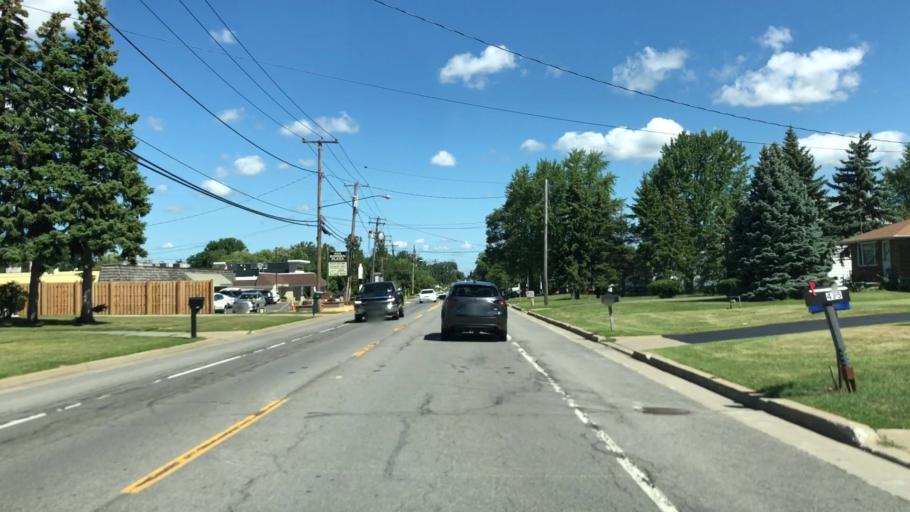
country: US
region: New York
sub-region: Erie County
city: Depew
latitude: 42.8662
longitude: -78.7089
